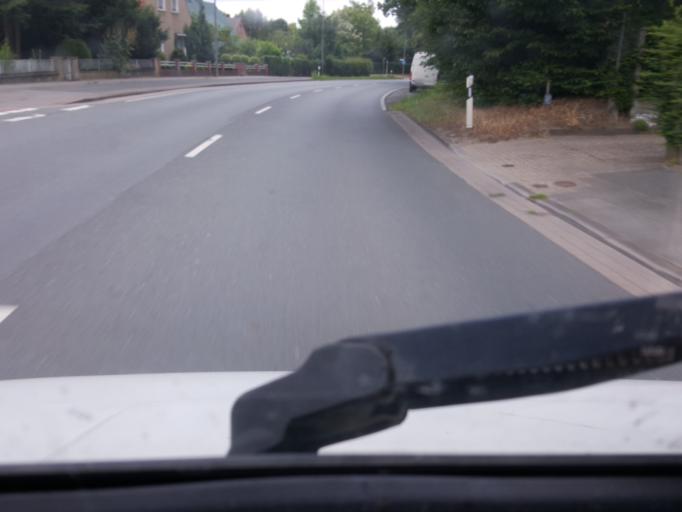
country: DE
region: North Rhine-Westphalia
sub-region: Regierungsbezirk Detmold
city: Minden
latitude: 52.3140
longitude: 8.9152
